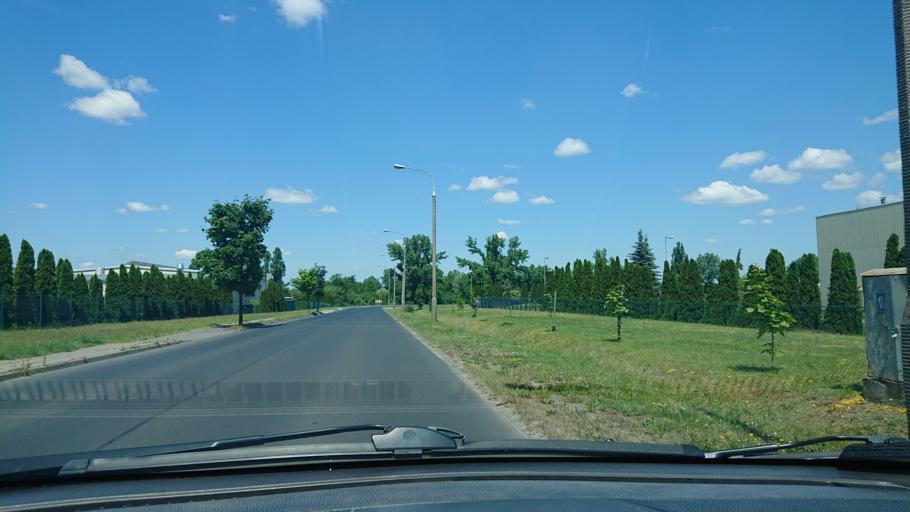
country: PL
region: Greater Poland Voivodeship
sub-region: Powiat gnieznienski
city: Gniezno
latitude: 52.5271
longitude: 17.6184
